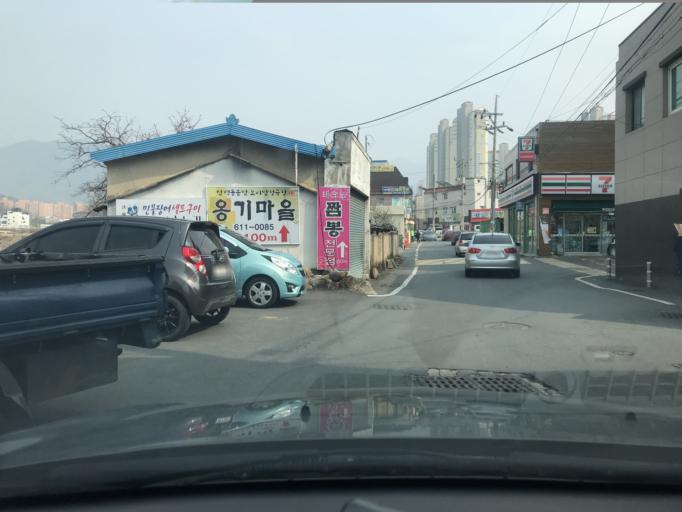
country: KR
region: Daegu
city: Hwawon
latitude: 35.6967
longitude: 128.4510
